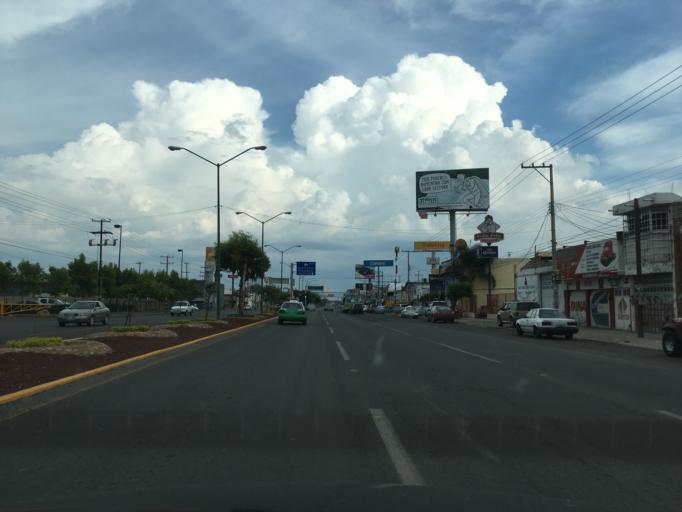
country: MX
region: Guanajuato
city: Celaya
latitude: 20.5451
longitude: -100.8214
